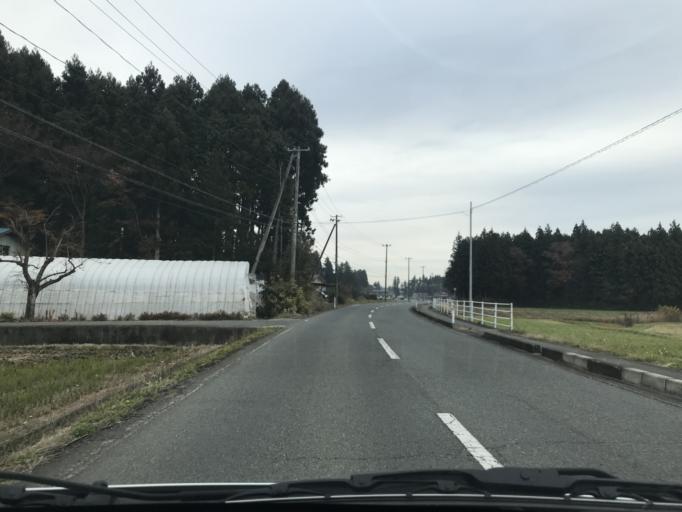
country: JP
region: Iwate
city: Mizusawa
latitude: 39.1067
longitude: 141.1073
